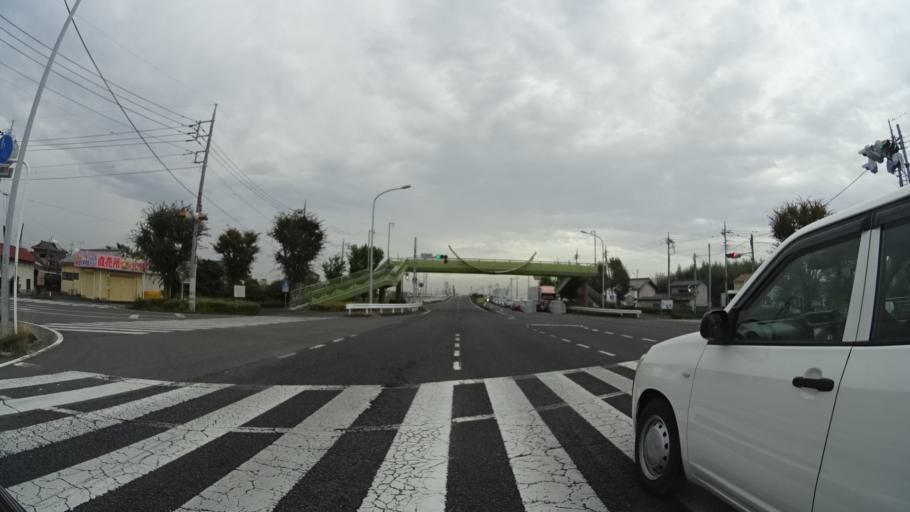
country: JP
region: Gunma
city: Maebashi-shi
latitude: 36.3732
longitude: 139.1289
